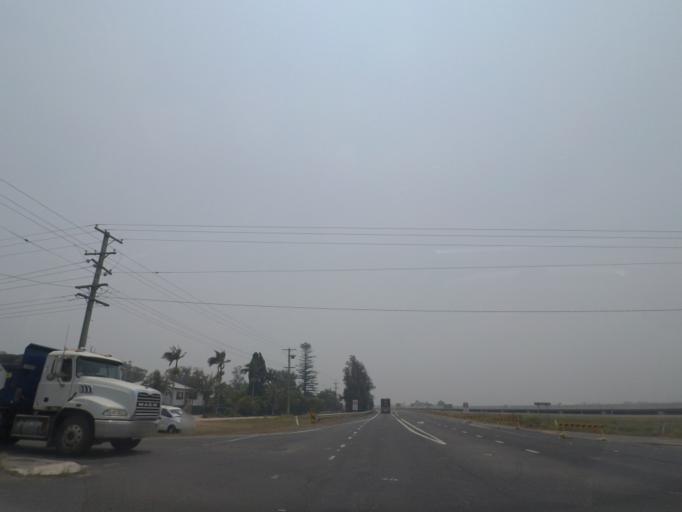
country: AU
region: New South Wales
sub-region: Clarence Valley
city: Maclean
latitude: -29.4189
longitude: 153.2407
